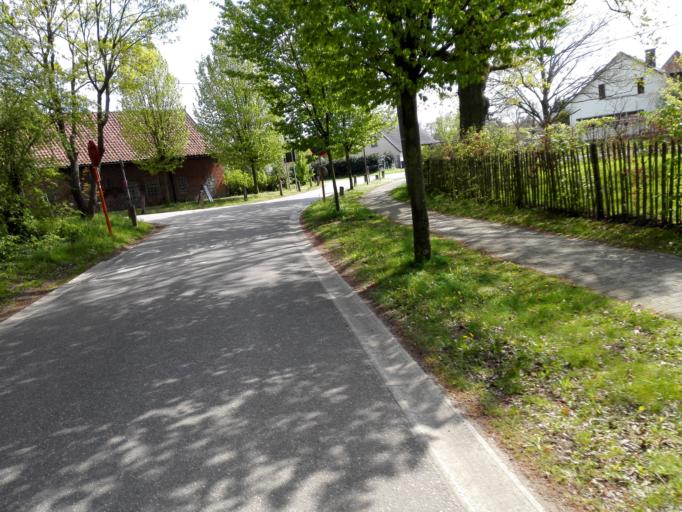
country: BE
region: Flanders
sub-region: Provincie Vlaams-Brabant
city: Rotselaar
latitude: 50.9577
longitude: 4.7209
